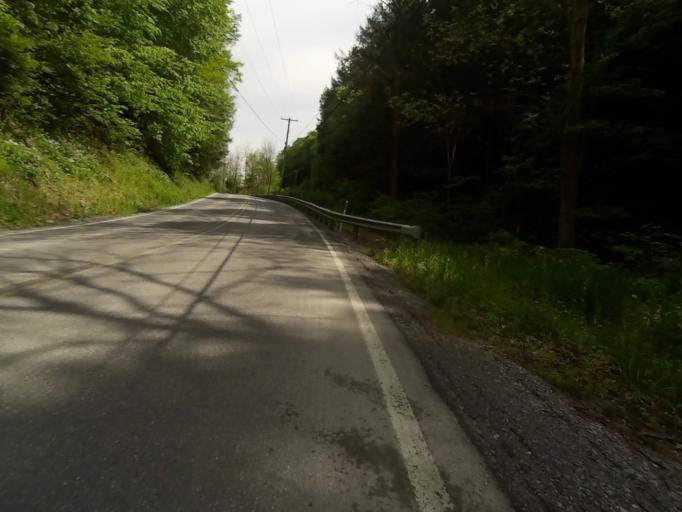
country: US
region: Pennsylvania
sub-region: Centre County
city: Zion
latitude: 40.9989
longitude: -77.6452
